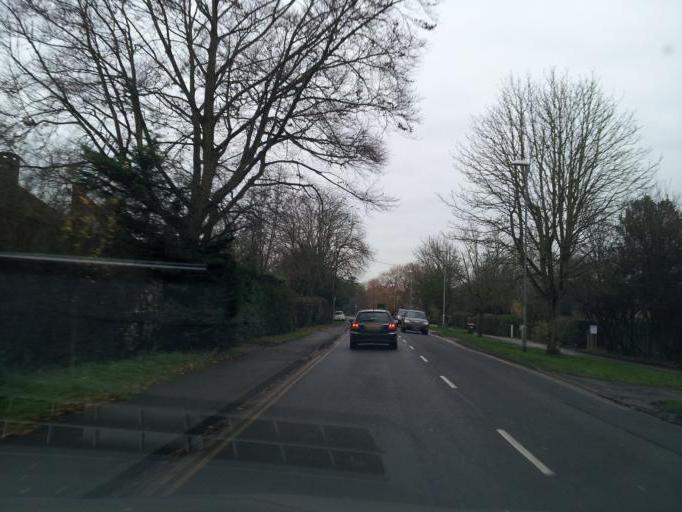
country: GB
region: England
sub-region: Cambridgeshire
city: Grantchester
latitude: 52.1982
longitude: 0.0973
